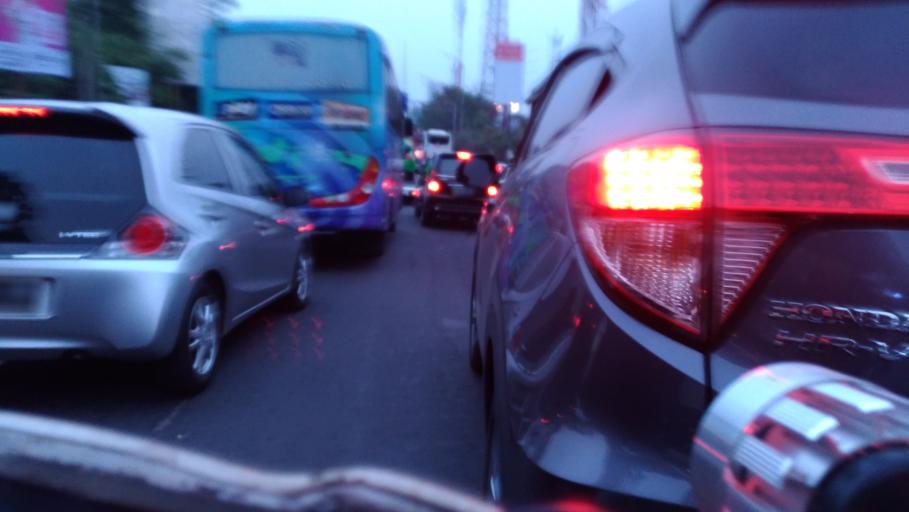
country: ID
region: West Java
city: Cileungsir
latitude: -6.3684
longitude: 106.8959
